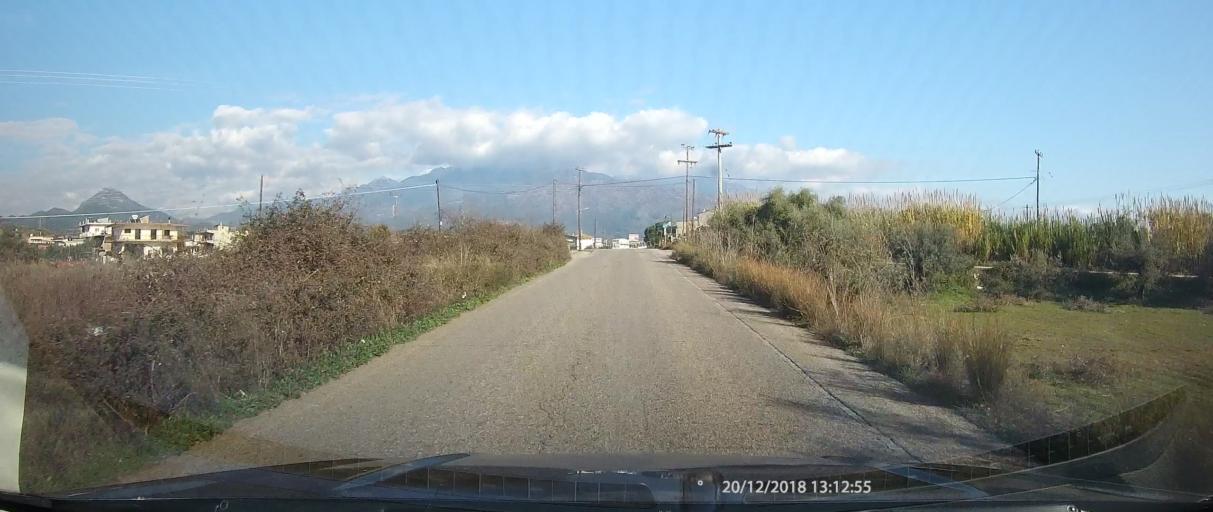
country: GR
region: West Greece
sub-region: Nomos Aitolias kai Akarnanias
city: Kainouryion
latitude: 38.6007
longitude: 21.4746
